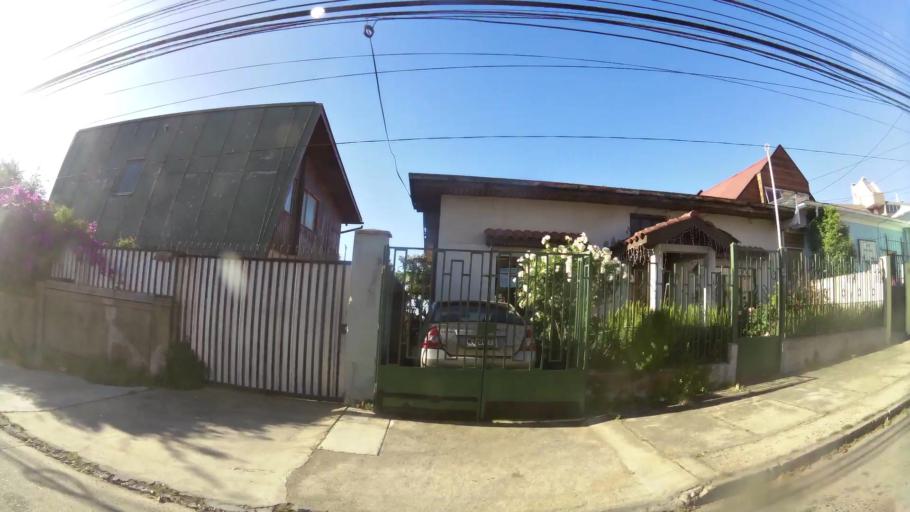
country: CL
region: Valparaiso
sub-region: Provincia de Valparaiso
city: Vina del Mar
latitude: -33.0301
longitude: -71.5698
